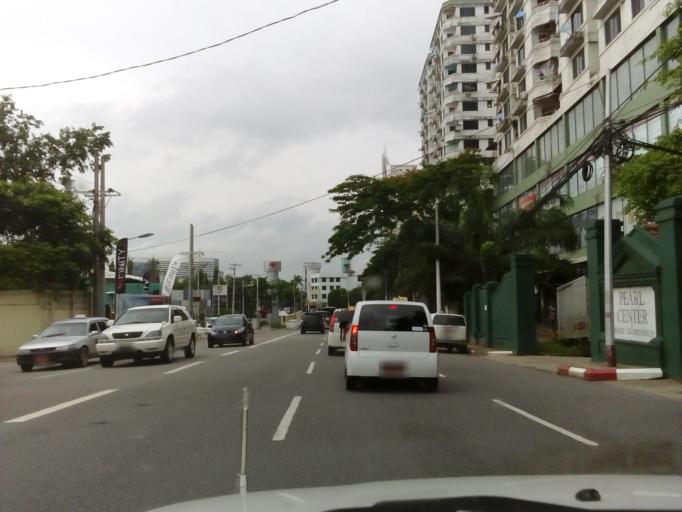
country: MM
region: Yangon
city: Yangon
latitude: 16.8164
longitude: 96.1562
